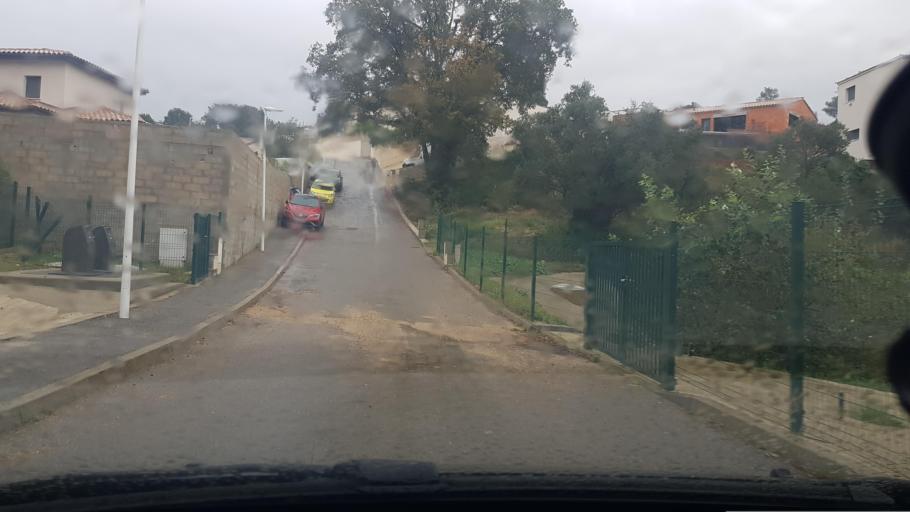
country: FR
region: Languedoc-Roussillon
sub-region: Departement du Gard
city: Bellegarde
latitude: 43.7549
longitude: 4.5040
